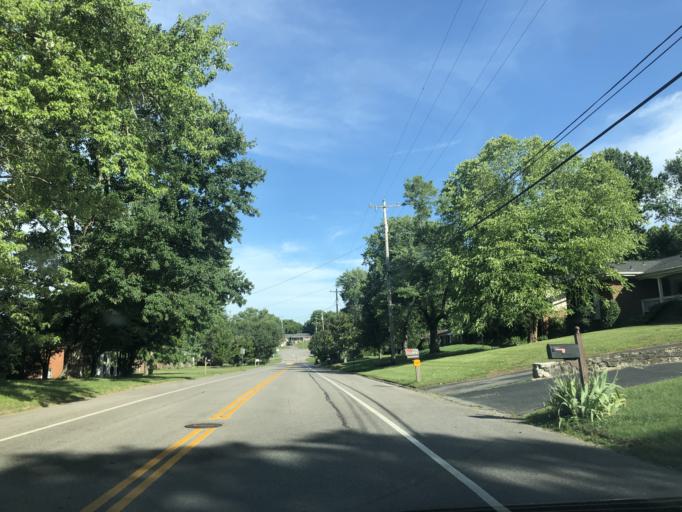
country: US
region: Tennessee
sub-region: Davidson County
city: Belle Meade
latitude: 36.0608
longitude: -86.9364
